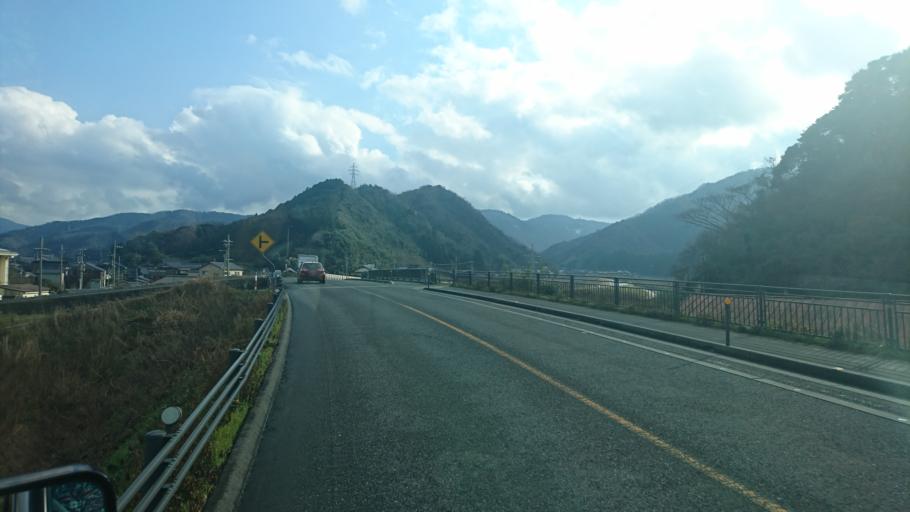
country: JP
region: Tottori
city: Tottori
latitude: 35.6089
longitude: 134.4702
